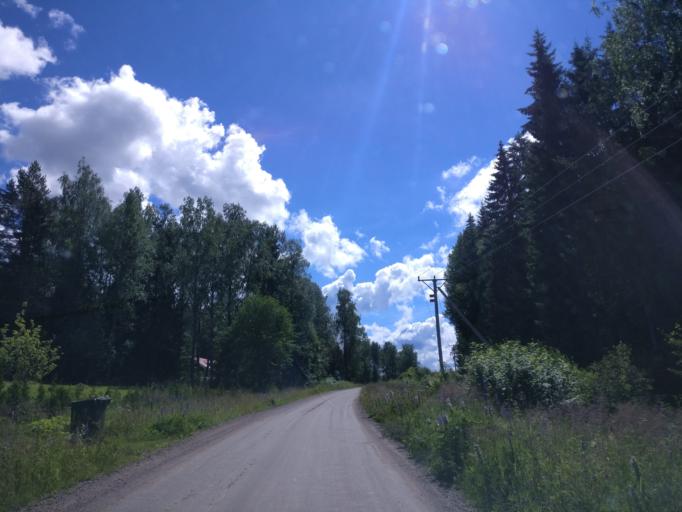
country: SE
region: Vaermland
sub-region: Hagfors Kommun
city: Hagfors
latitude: 60.0355
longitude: 13.6674
